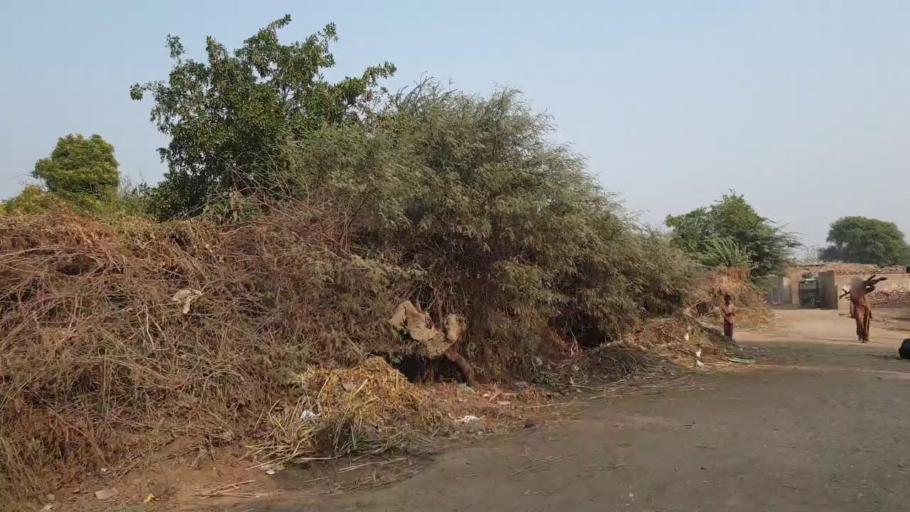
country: PK
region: Sindh
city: Tando Muhammad Khan
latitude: 25.1434
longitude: 68.6138
